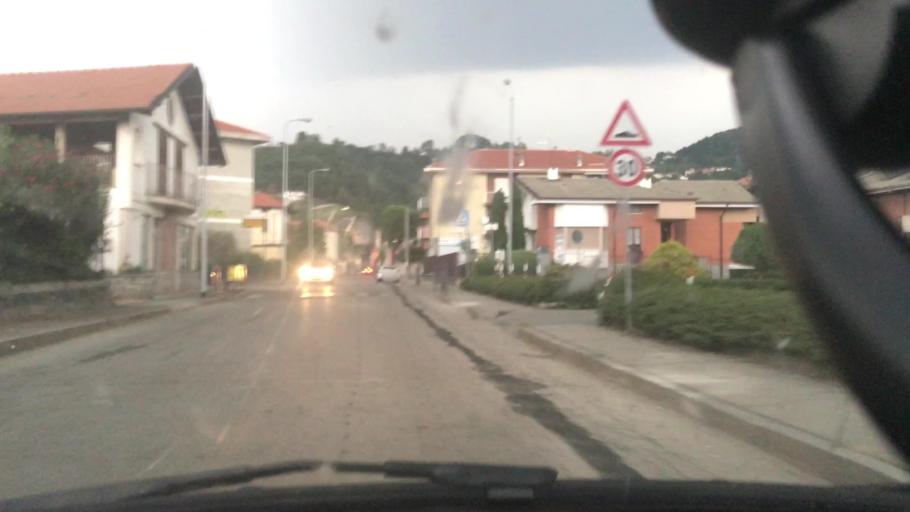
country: IT
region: Piedmont
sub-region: Provincia di Biella
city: Ronco Biellese
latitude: 45.5705
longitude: 8.0759
